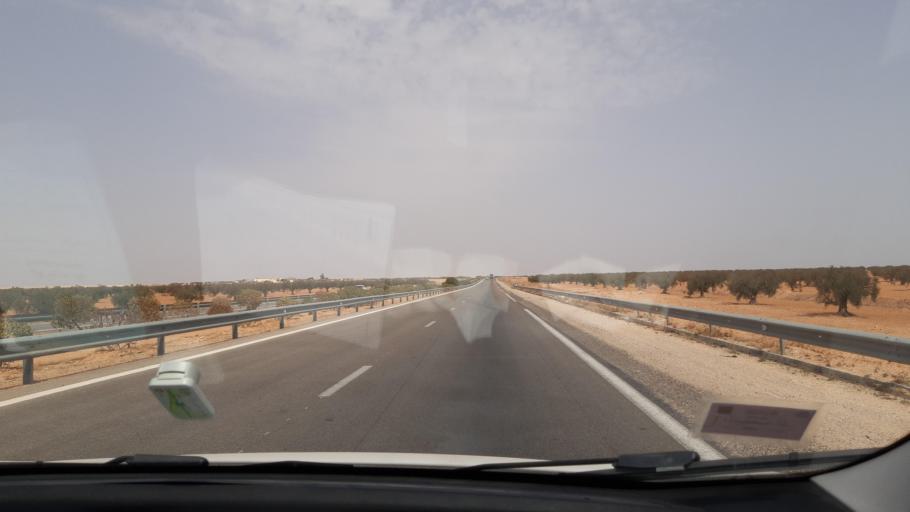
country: TN
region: Safaqis
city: Bi'r `Ali Bin Khalifah
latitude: 34.5602
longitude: 10.3386
